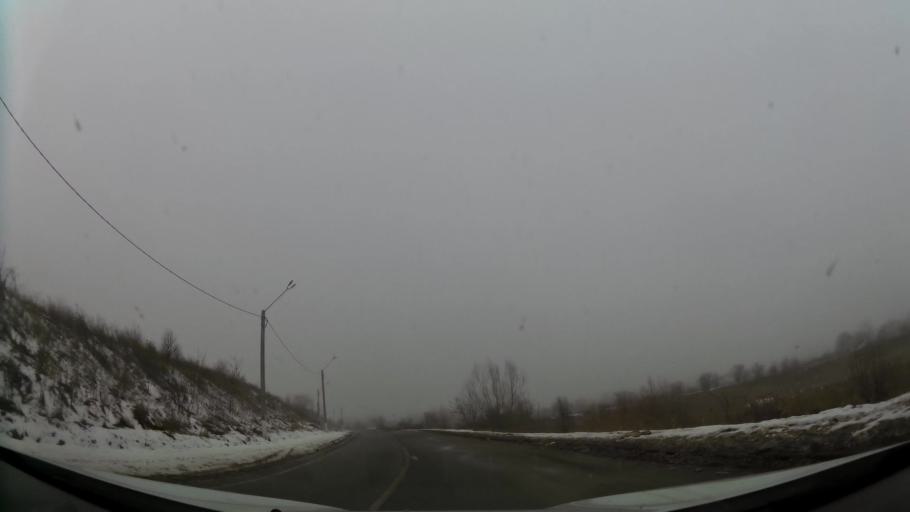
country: RO
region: Ilfov
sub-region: Comuna Chiajna
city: Chiajna
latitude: 44.4616
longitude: 25.9934
